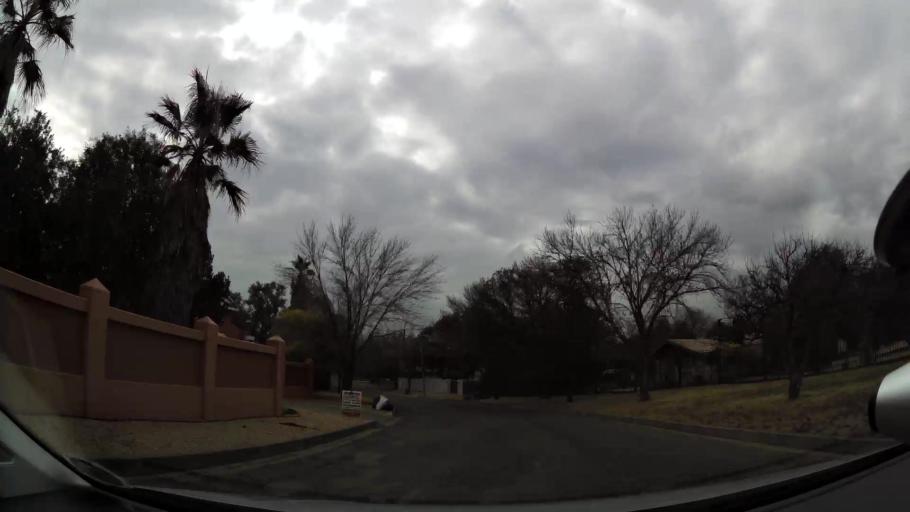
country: ZA
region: Orange Free State
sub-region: Fezile Dabi District Municipality
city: Kroonstad
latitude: -27.6769
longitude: 27.2477
